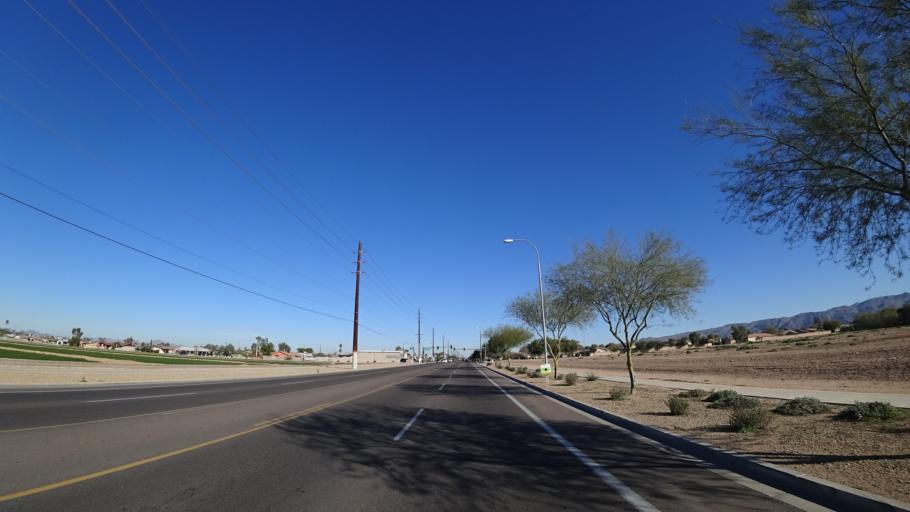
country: US
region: Arizona
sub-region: Maricopa County
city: Laveen
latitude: 33.3922
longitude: -112.1099
